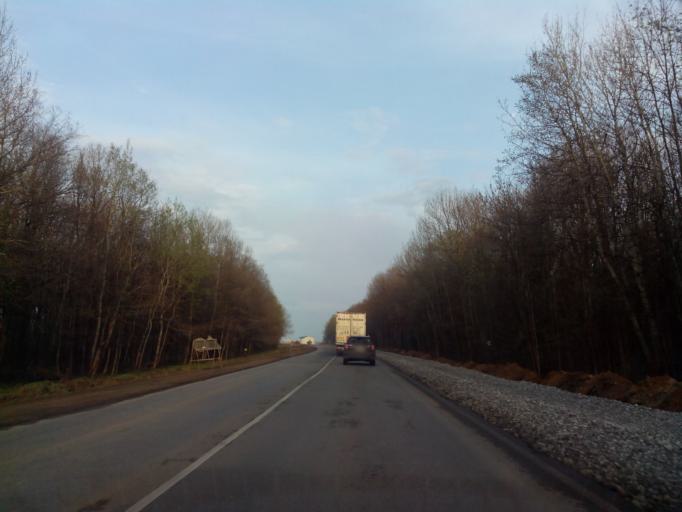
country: RU
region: Rjazan
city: Zarechnyy
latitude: 53.7532
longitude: 39.7976
